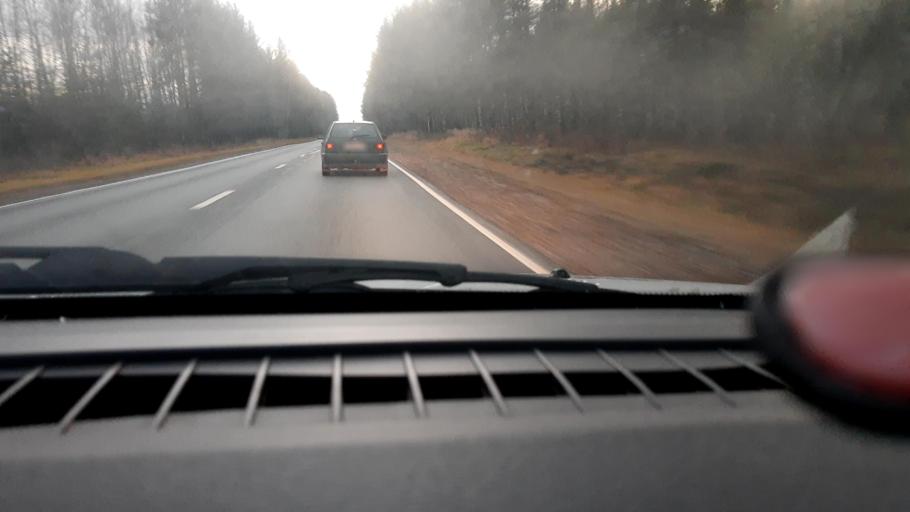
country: RU
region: Nizjnij Novgorod
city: Krasnyye Baki
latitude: 57.0420
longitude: 45.1295
